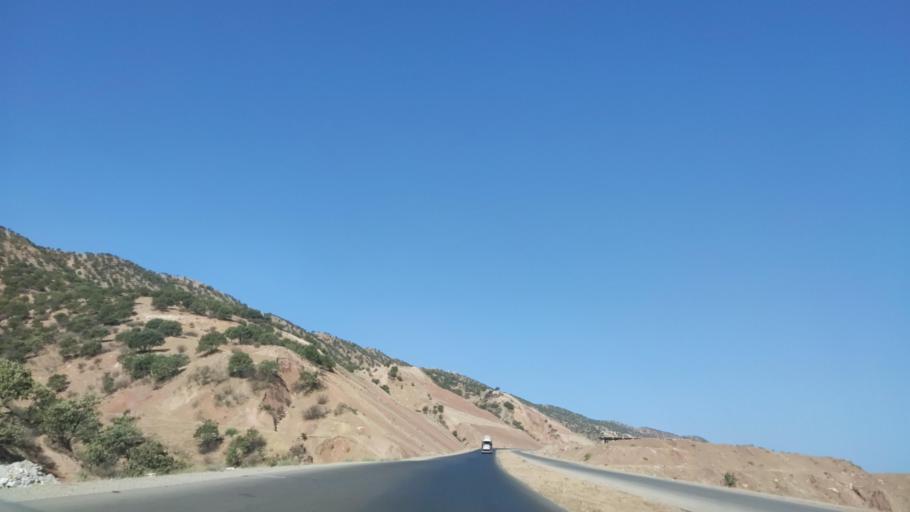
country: IQ
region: Arbil
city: Shaqlawah
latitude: 36.4327
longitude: 44.3079
